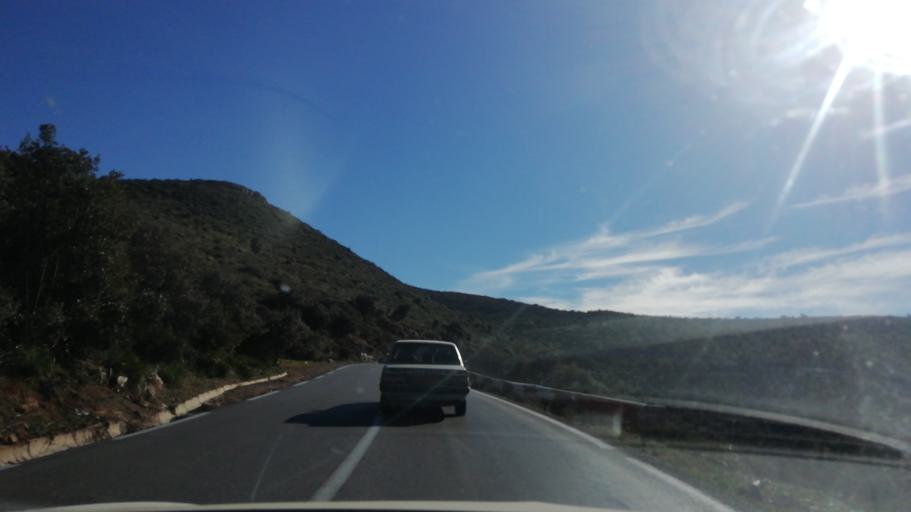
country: DZ
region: Tlemcen
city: Mansoura
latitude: 34.8470
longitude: -1.3635
